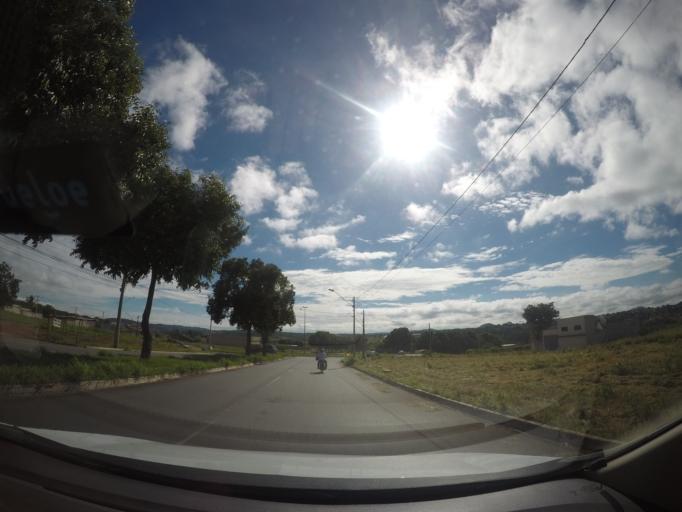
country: BR
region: Goias
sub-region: Goiania
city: Goiania
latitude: -16.6527
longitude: -49.1737
